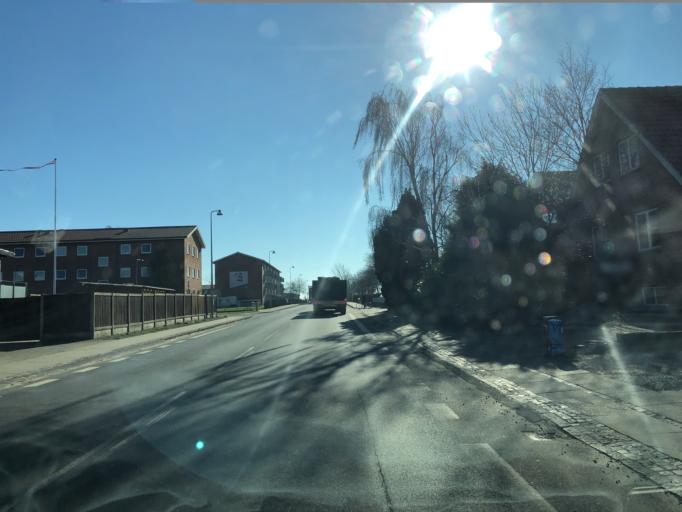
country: DK
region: Central Jutland
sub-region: Ikast-Brande Kommune
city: Ikast
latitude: 56.1398
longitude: 9.1644
